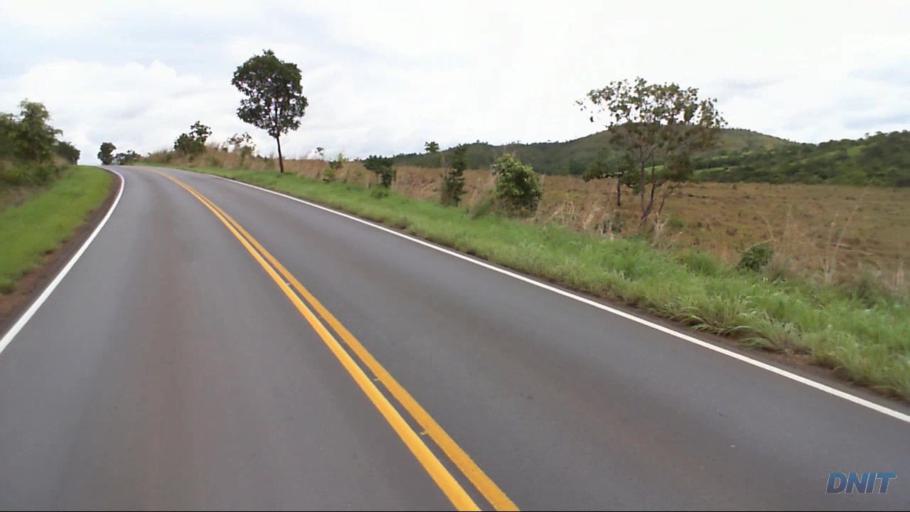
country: BR
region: Goias
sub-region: Padre Bernardo
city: Padre Bernardo
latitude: -15.4334
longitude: -48.1931
